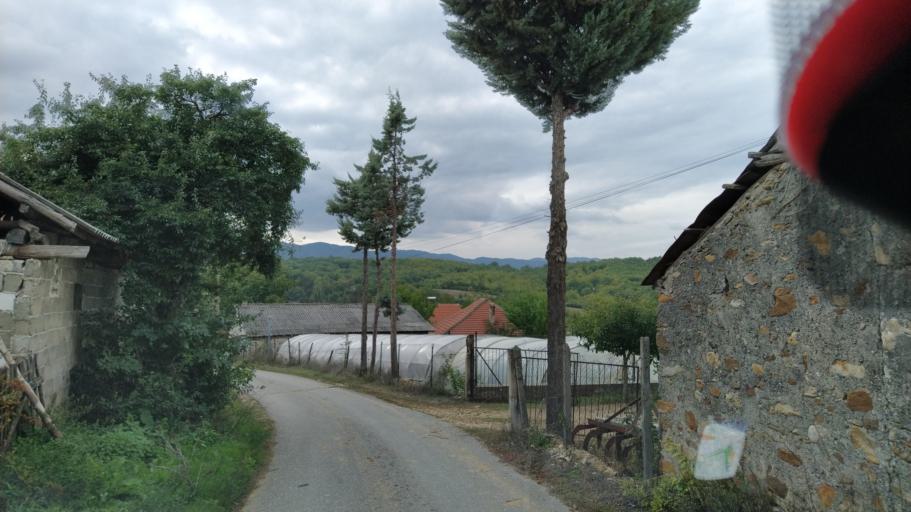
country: MK
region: Konce
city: Konce
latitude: 41.5050
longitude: 22.4588
